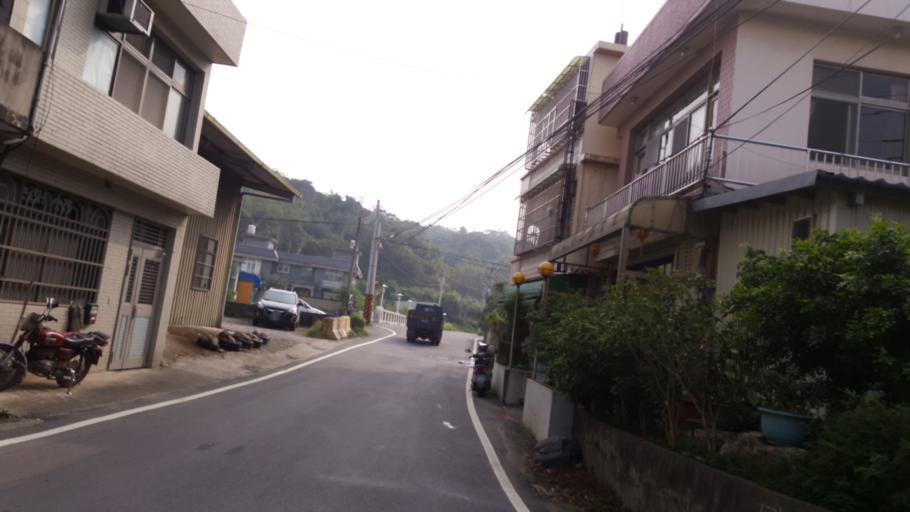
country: TW
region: Taiwan
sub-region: Hsinchu
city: Hsinchu
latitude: 24.7305
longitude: 120.9645
